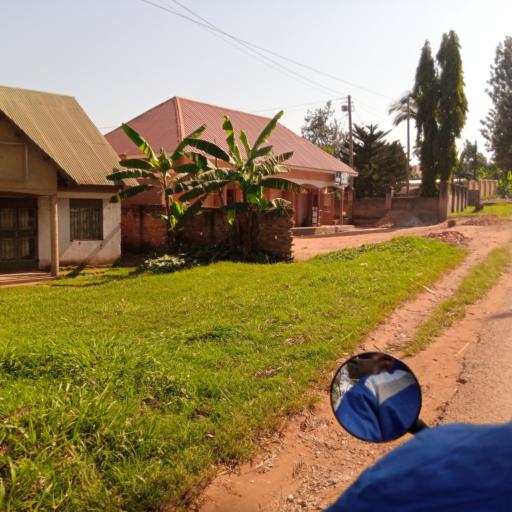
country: UG
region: Central Region
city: Masaka
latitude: -0.3468
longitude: 31.7272
